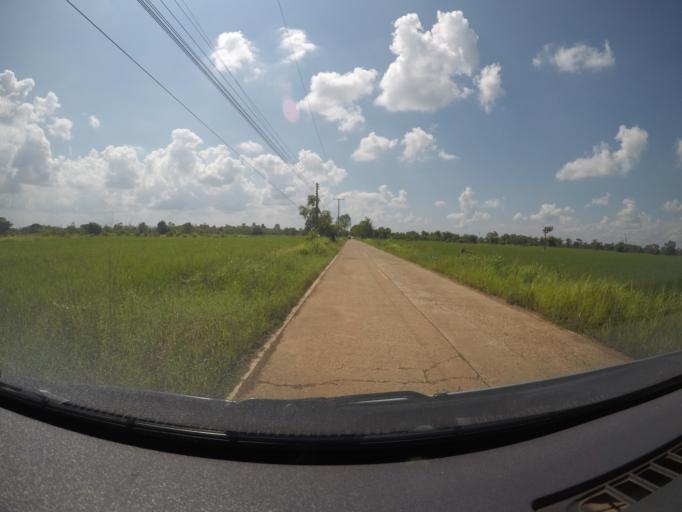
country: TH
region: Sakon Nakhon
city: Sakon Nakhon
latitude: 17.2116
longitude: 104.1209
